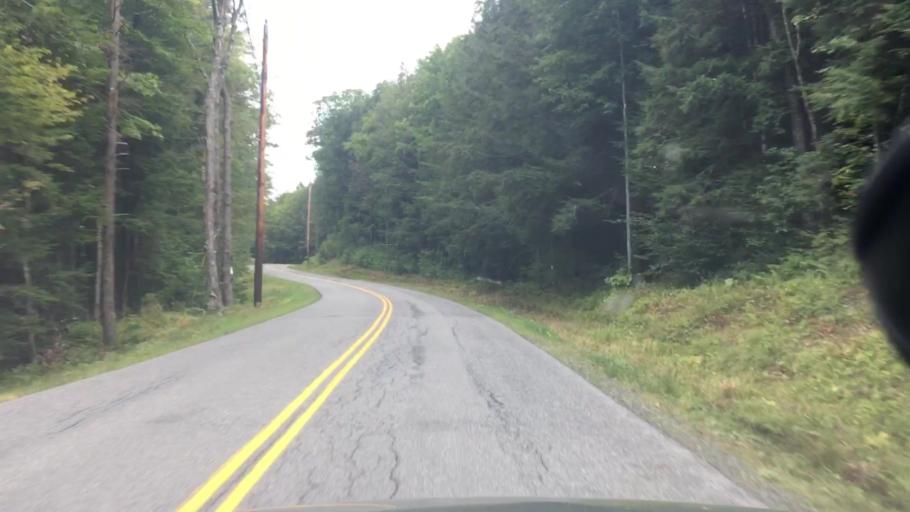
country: US
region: Vermont
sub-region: Windham County
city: Dover
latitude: 42.8092
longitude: -72.7659
